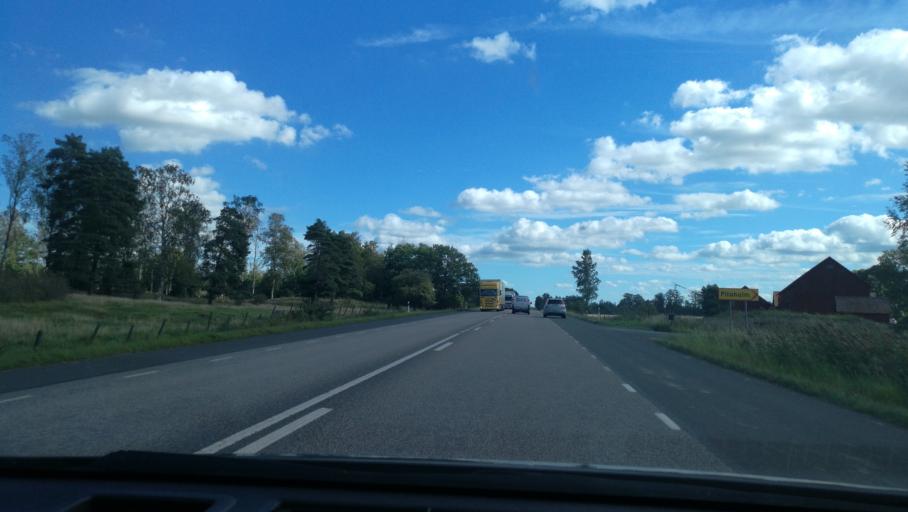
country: SE
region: Vaestra Goetaland
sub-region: Gotene Kommun
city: Kallby
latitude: 58.5114
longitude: 13.3508
